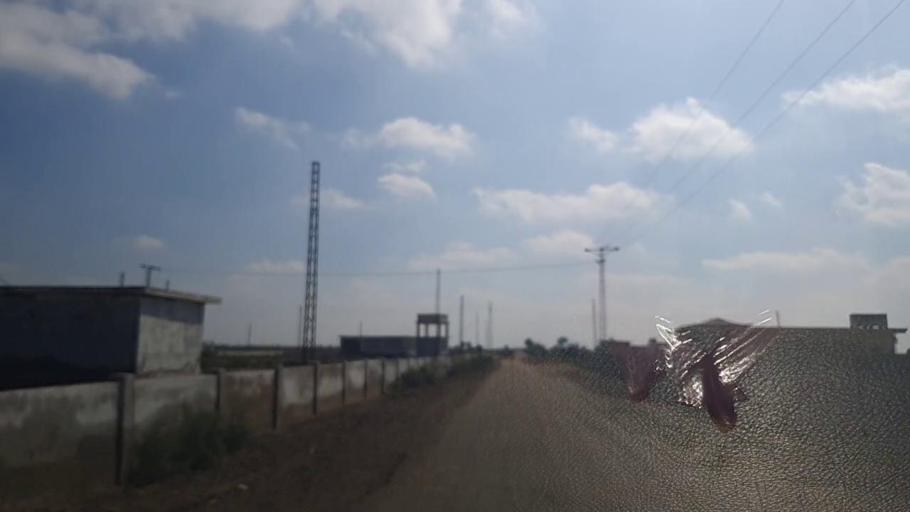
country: PK
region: Sindh
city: Sanghar
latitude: 26.0650
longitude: 69.0045
